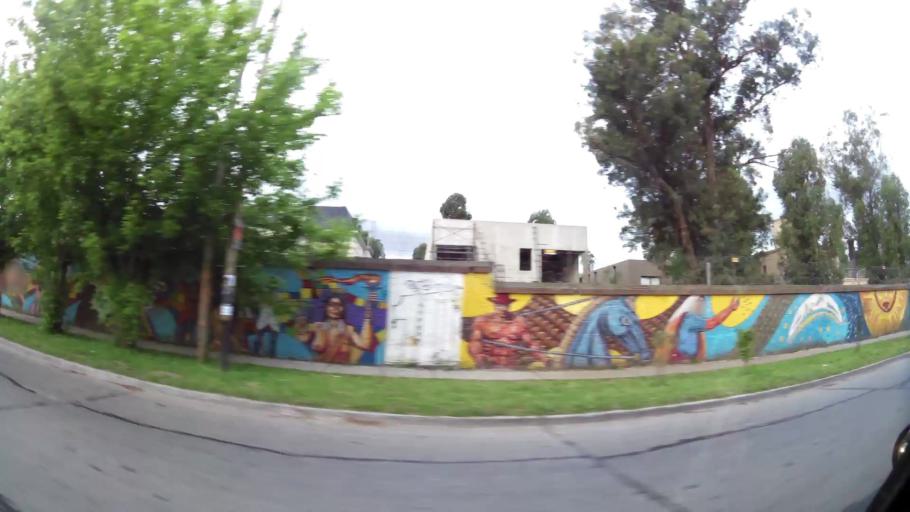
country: AR
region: Buenos Aires
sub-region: Partido de Quilmes
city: Quilmes
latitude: -34.7321
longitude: -58.2453
